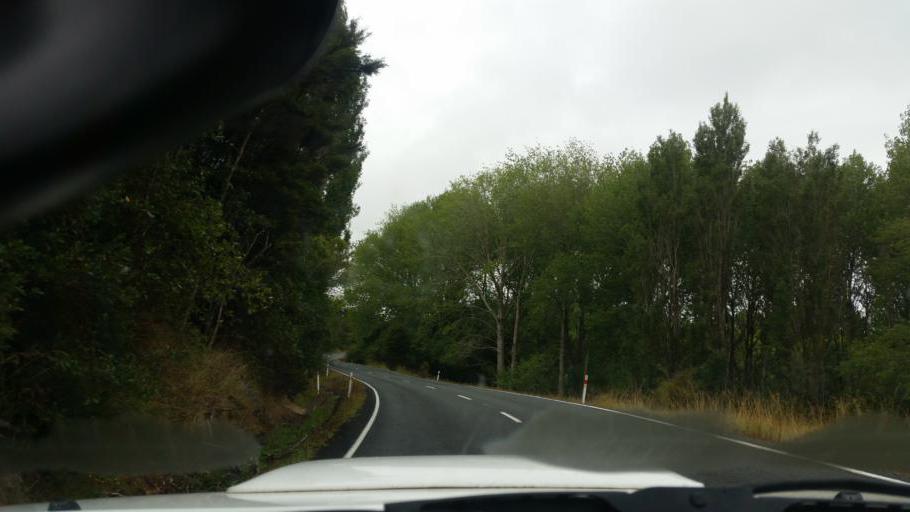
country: NZ
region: Auckland
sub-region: Auckland
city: Wellsford
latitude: -36.1541
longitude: 174.4672
